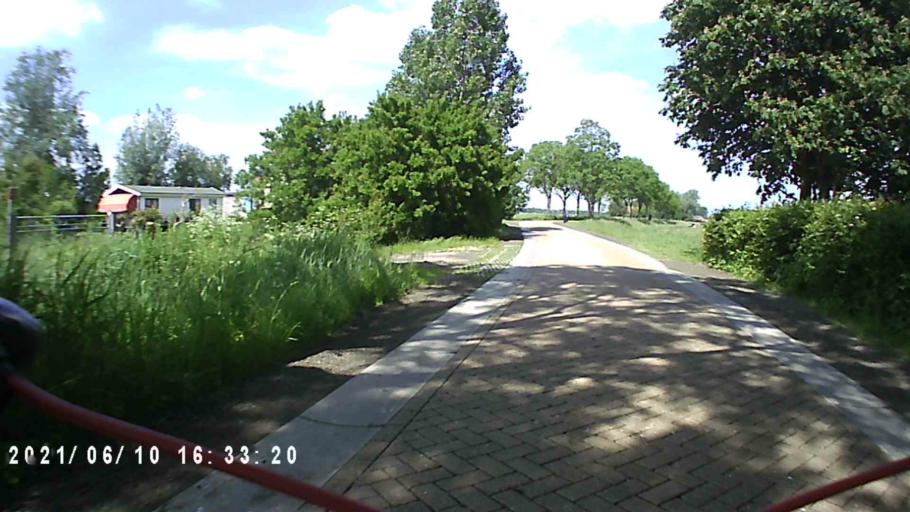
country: NL
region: Friesland
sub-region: Gemeente Achtkarspelen
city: Buitenpost
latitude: 53.2302
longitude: 6.1300
